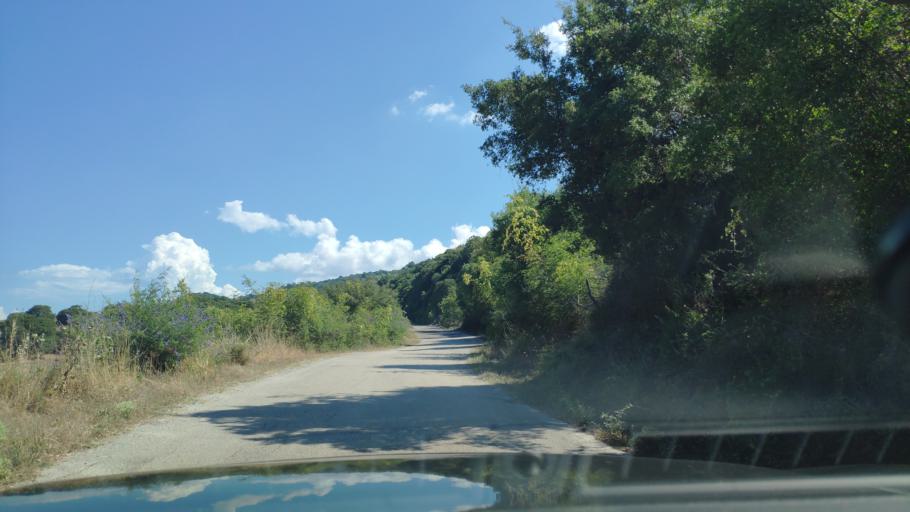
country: GR
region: West Greece
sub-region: Nomos Aitolias kai Akarnanias
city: Katouna
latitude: 38.8213
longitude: 21.1031
